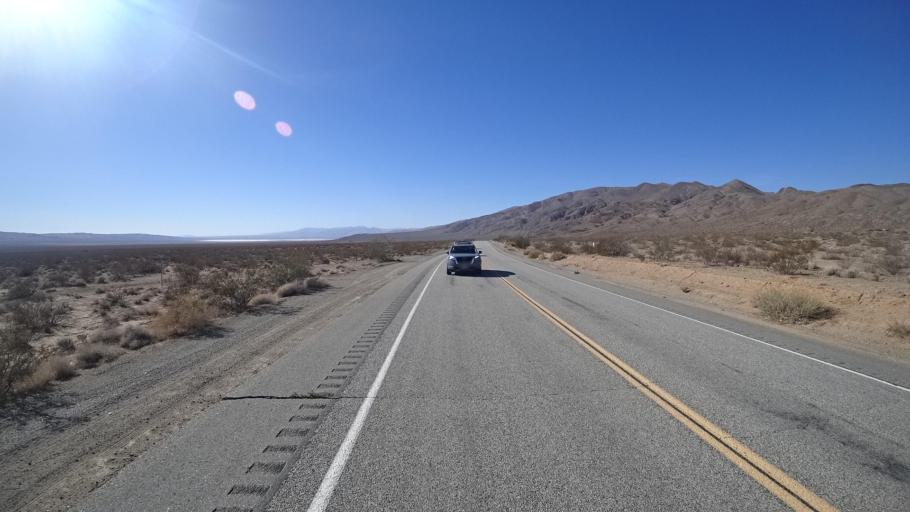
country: US
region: California
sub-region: Kern County
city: Ridgecrest
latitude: 35.4190
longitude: -117.7518
